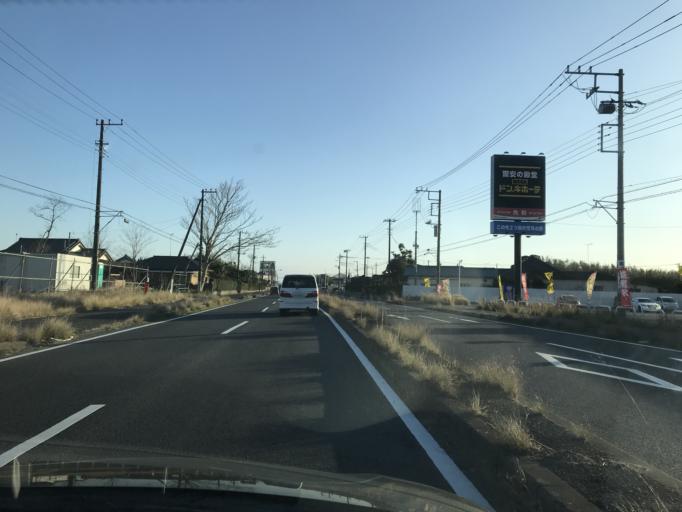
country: JP
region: Chiba
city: Omigawa
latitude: 35.8981
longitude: 140.6339
